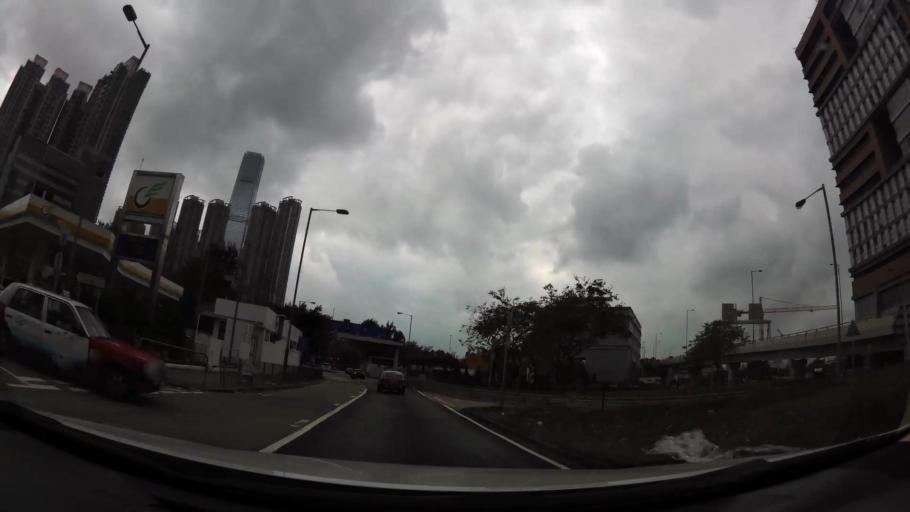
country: HK
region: Kowloon City
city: Kowloon
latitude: 22.3120
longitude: 114.1661
